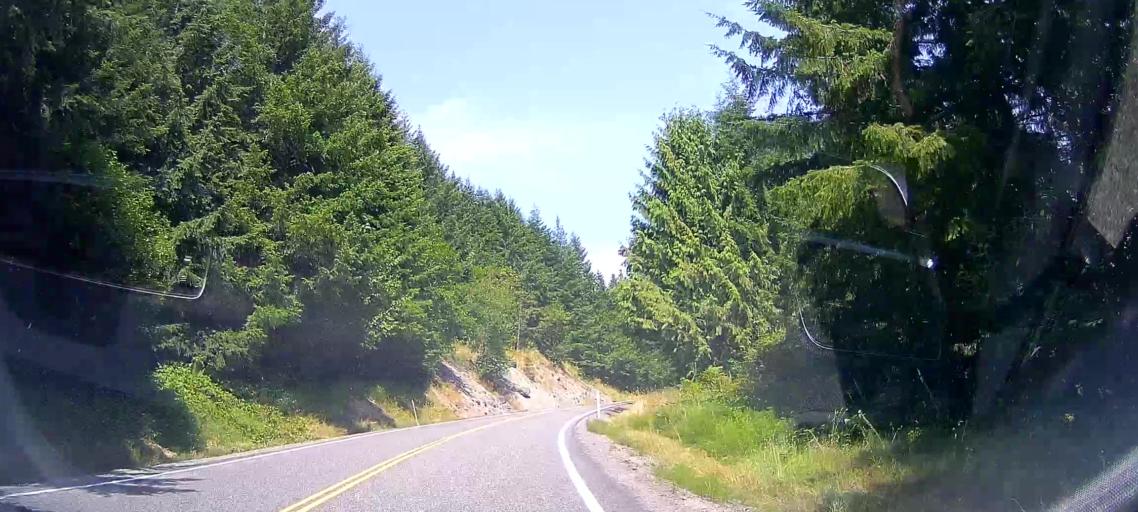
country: US
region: Washington
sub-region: Snohomish County
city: Bryant
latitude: 48.3370
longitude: -122.1236
